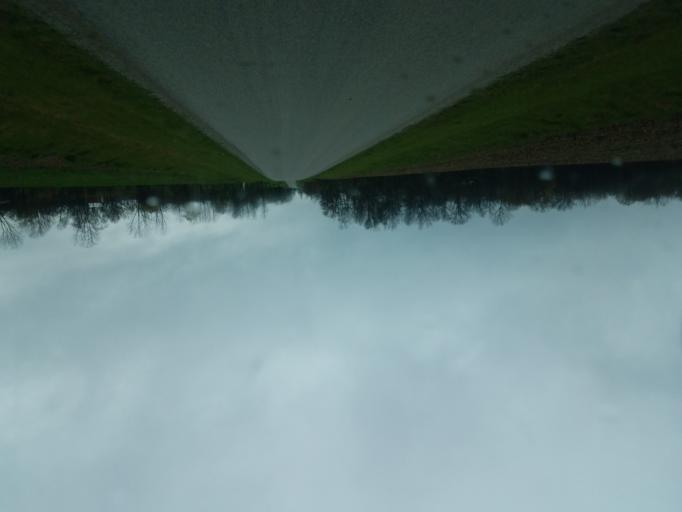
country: US
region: Ohio
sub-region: Morrow County
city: Mount Gilead
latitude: 40.4443
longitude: -82.7529
